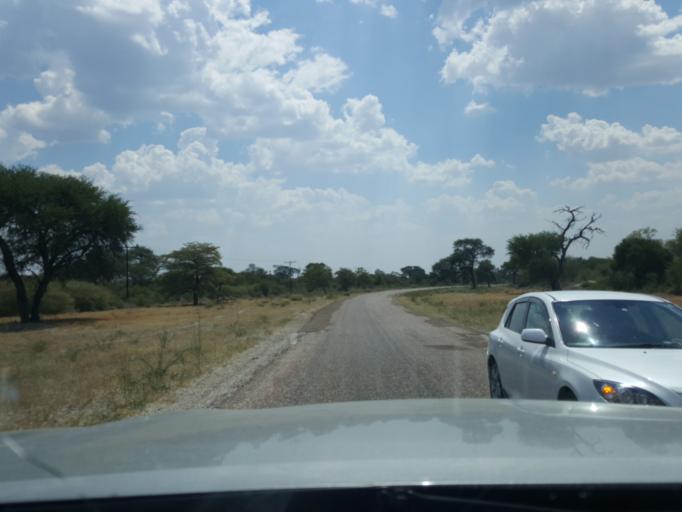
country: BW
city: Tsau
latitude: -19.9819
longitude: 22.2570
